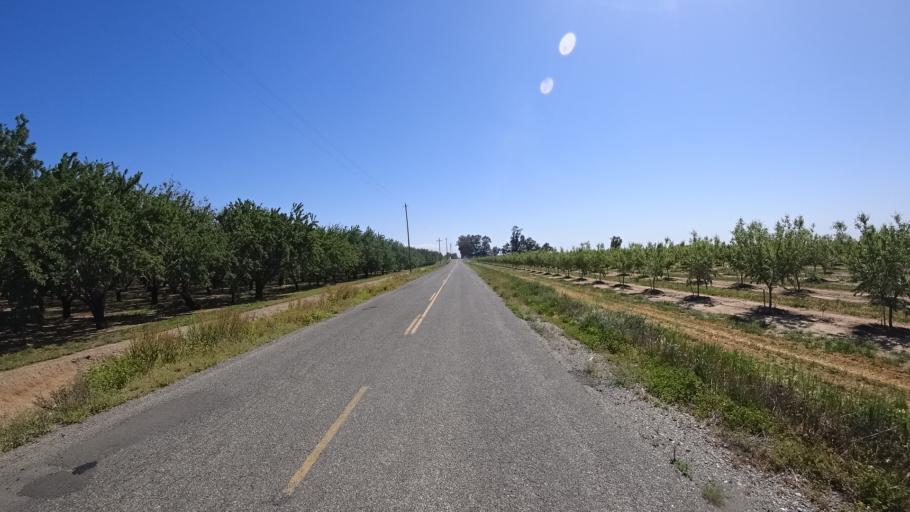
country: US
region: California
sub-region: Glenn County
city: Orland
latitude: 39.6968
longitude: -122.1910
